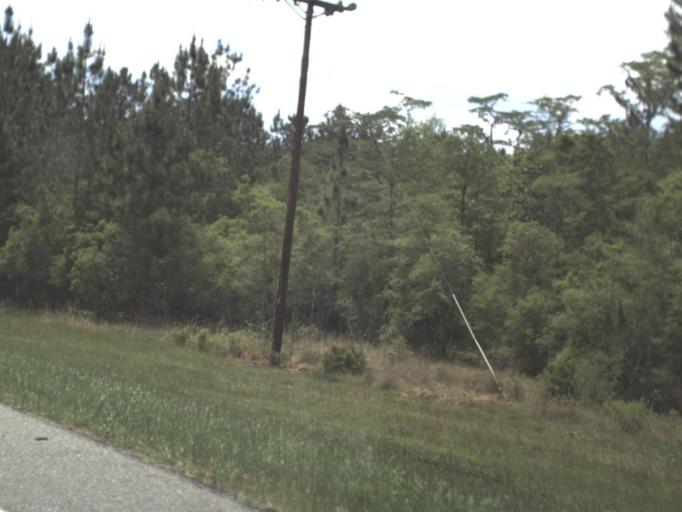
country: US
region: Florida
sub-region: Calhoun County
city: Blountstown
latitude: 30.3464
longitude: -85.1143
